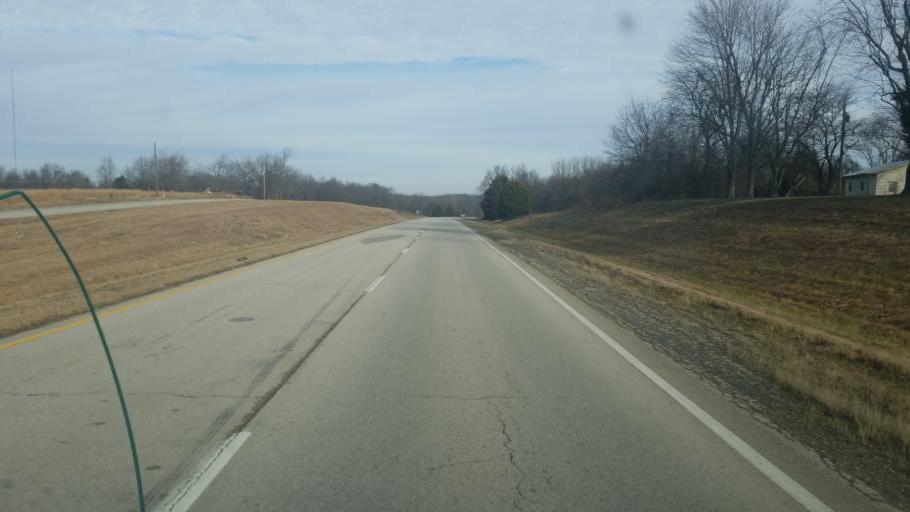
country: US
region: Missouri
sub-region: Stoddard County
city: Bloomfield
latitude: 36.8515
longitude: -89.9396
